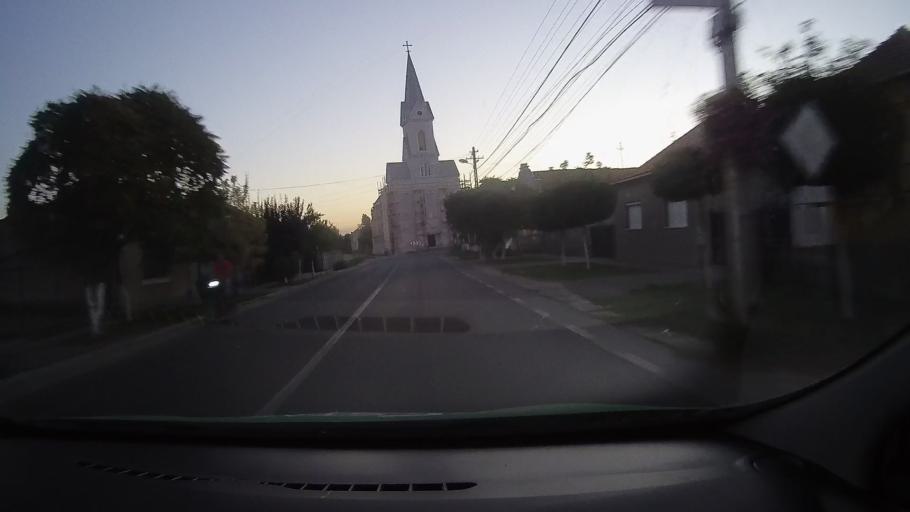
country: RO
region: Bihor
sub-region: Comuna Valea lui Mihai
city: Valea lui Mihai
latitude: 47.5145
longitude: 22.1308
